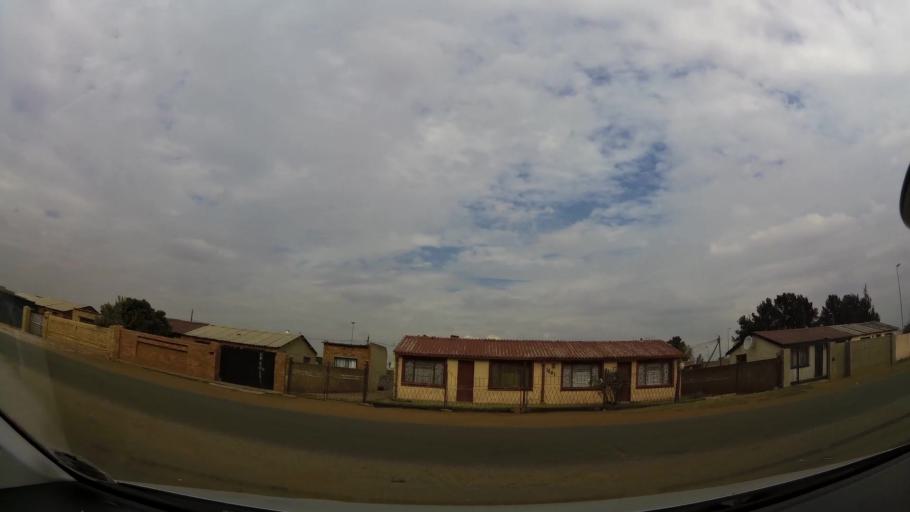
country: ZA
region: Gauteng
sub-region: City of Johannesburg Metropolitan Municipality
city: Soweto
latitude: -26.2630
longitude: 27.8578
